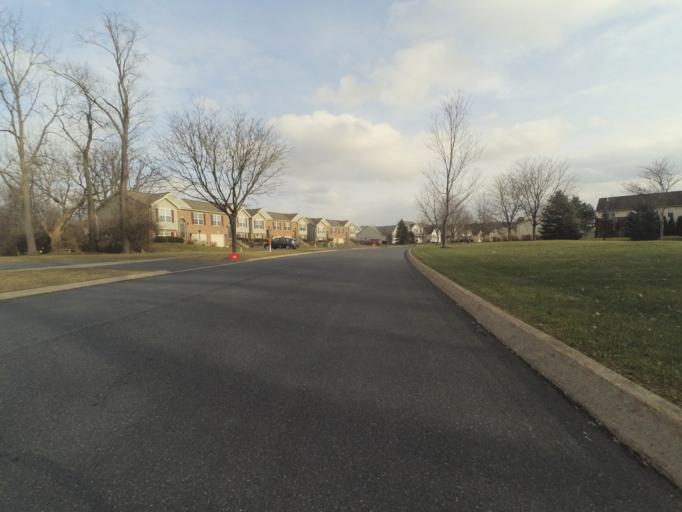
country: US
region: Pennsylvania
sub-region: Centre County
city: Park Forest Village
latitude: 40.7873
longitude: -77.8989
